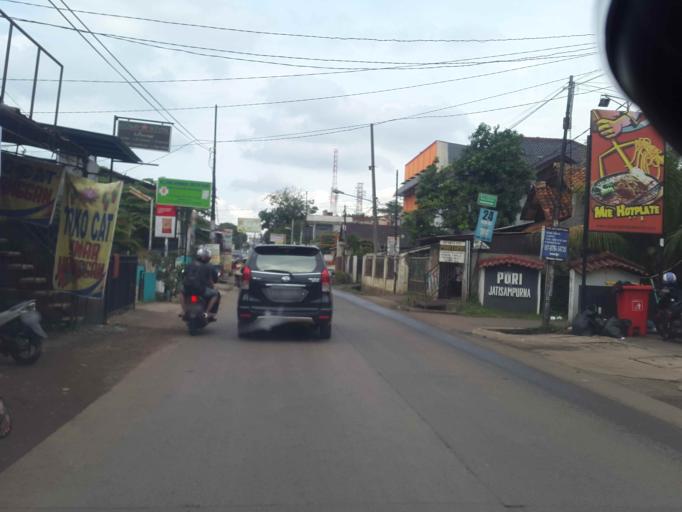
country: ID
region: West Java
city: Cileungsir
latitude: -6.3482
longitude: 106.9224
